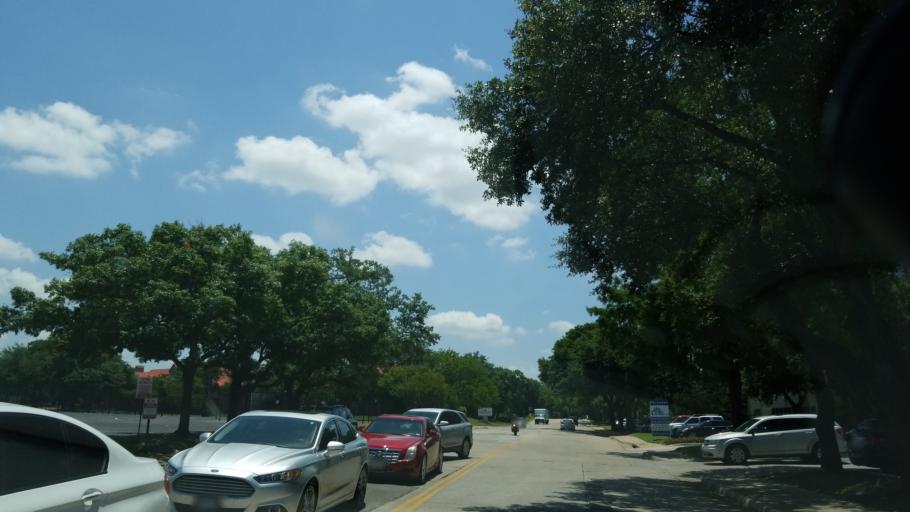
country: US
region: Texas
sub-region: Dallas County
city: Dallas
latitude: 32.8200
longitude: -96.8663
